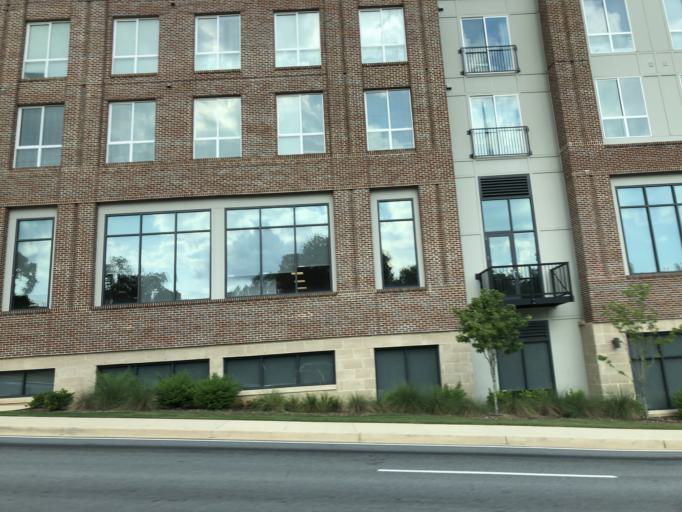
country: US
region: Georgia
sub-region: Clarke County
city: Athens
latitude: 33.9563
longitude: -83.3697
